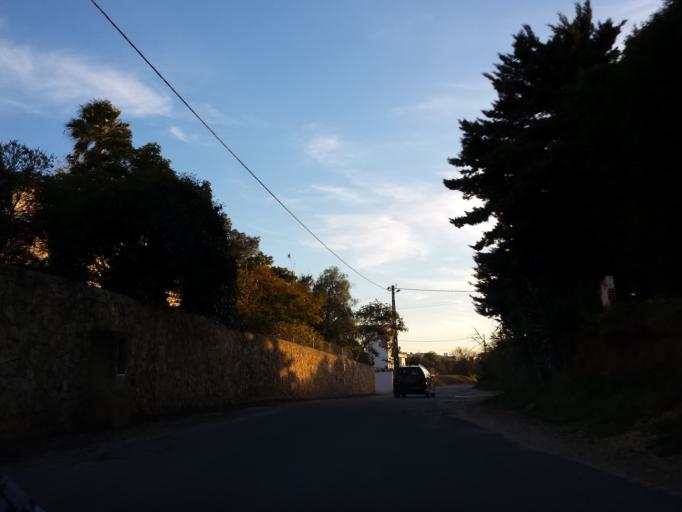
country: PT
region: Faro
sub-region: Lagos
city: Lagos
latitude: 37.1183
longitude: -8.6663
